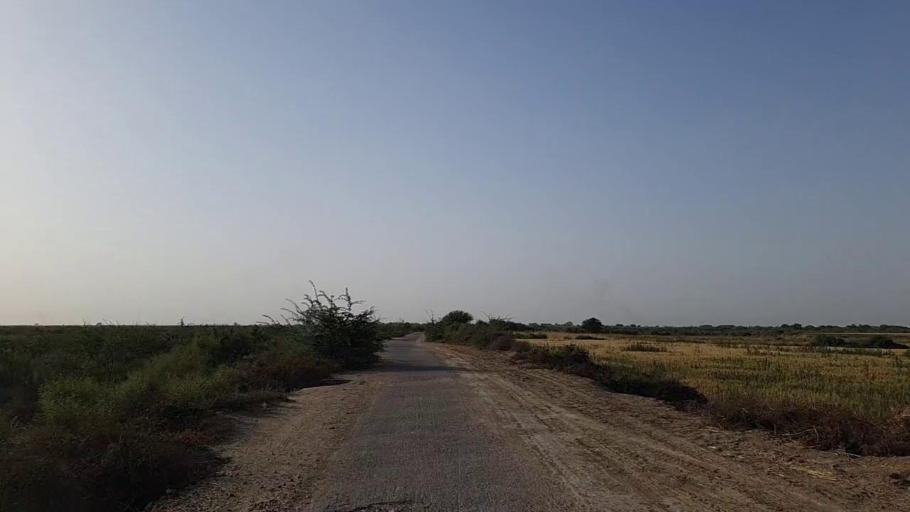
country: PK
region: Sindh
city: Jati
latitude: 24.3036
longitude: 68.1683
